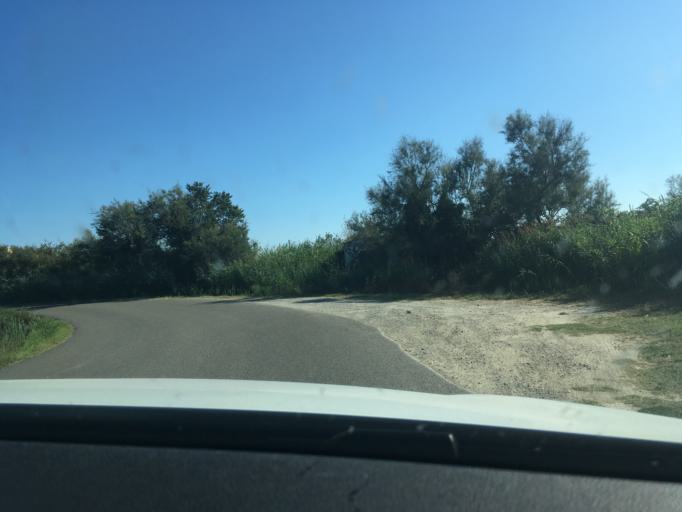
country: FR
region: Provence-Alpes-Cote d'Azur
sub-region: Departement des Bouches-du-Rhone
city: Saintes-Maries-de-la-Mer
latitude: 43.5465
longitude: 4.3450
